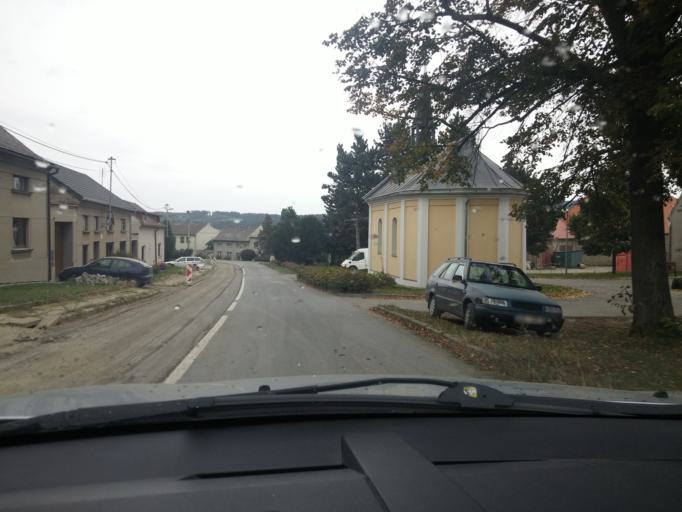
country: CZ
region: Olomoucky
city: Namest' na Hane
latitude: 49.5795
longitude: 17.0468
